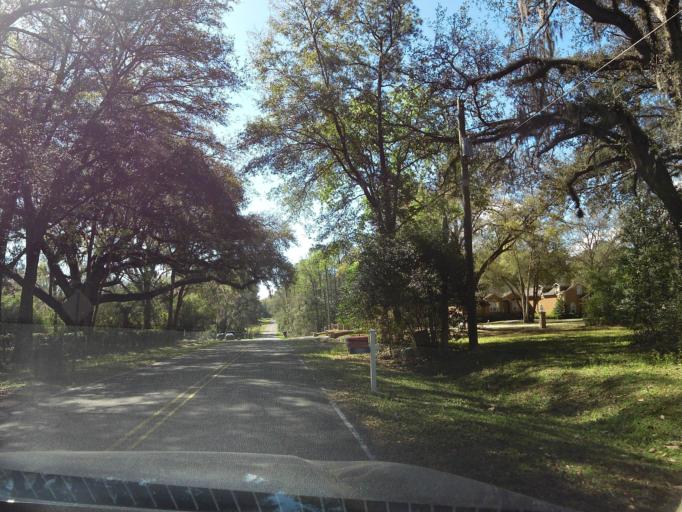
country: US
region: Florida
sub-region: Clay County
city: Green Cove Springs
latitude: 29.9827
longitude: -81.7060
